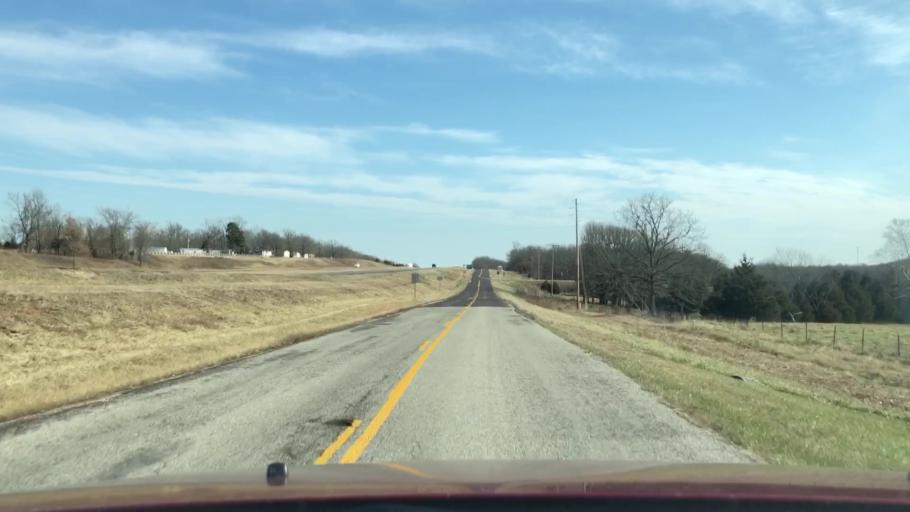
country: US
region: Missouri
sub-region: Wright County
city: Mansfield
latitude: 37.1122
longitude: -92.6324
